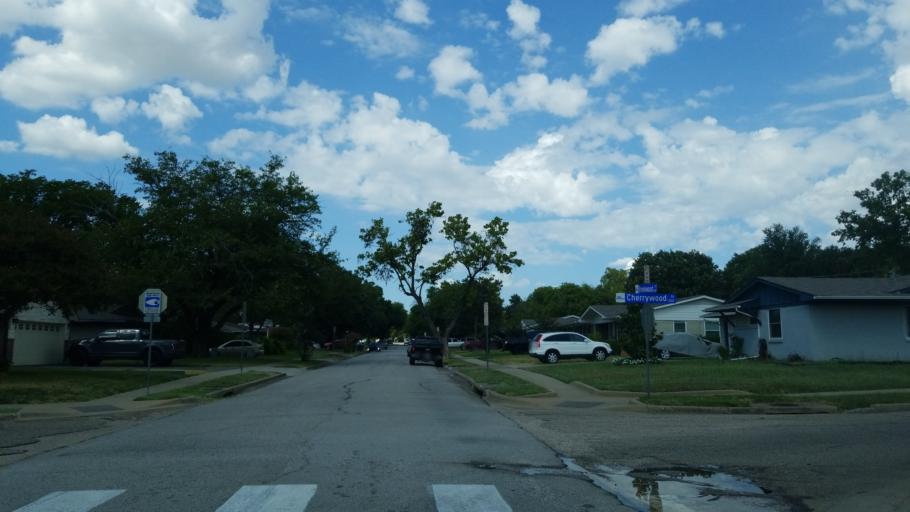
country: US
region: Texas
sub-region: Dallas County
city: Richardson
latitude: 32.9538
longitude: -96.7651
